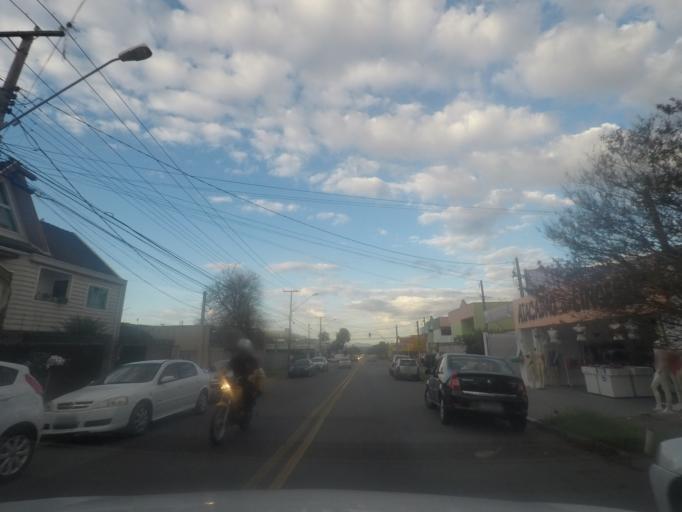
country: BR
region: Parana
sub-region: Pinhais
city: Pinhais
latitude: -25.4681
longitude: -49.2098
